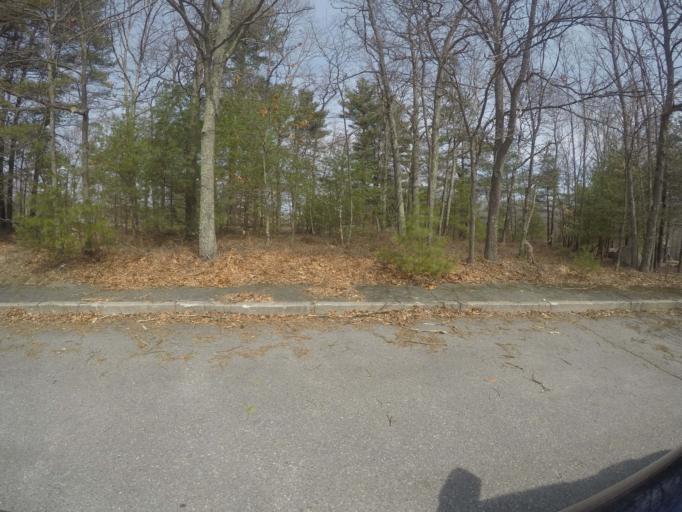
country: US
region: Massachusetts
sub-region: Bristol County
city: Easton
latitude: 42.0510
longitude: -71.1099
